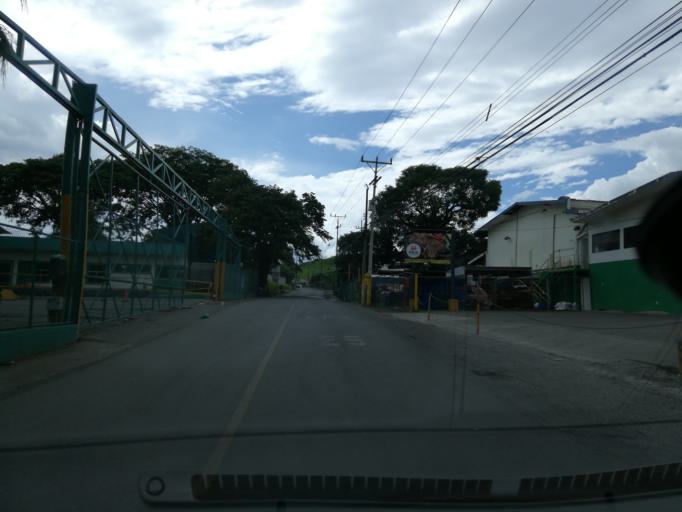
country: CR
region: Alajuela
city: Alajuela
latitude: 9.9959
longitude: -84.2191
